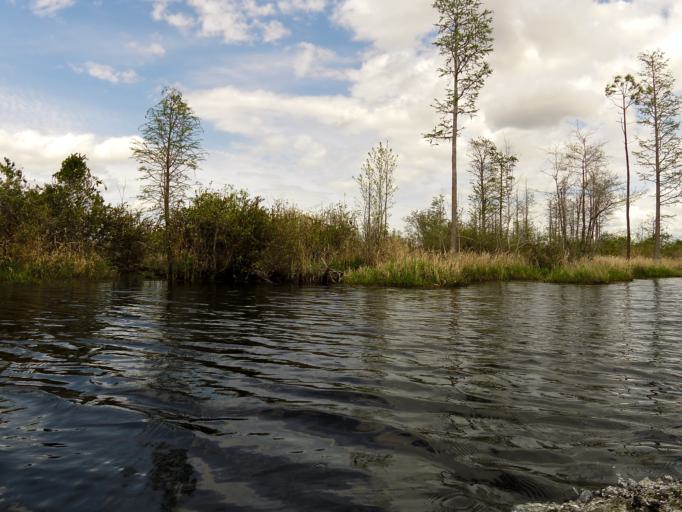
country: US
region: Georgia
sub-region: Charlton County
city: Folkston
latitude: 30.7365
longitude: -82.1479
